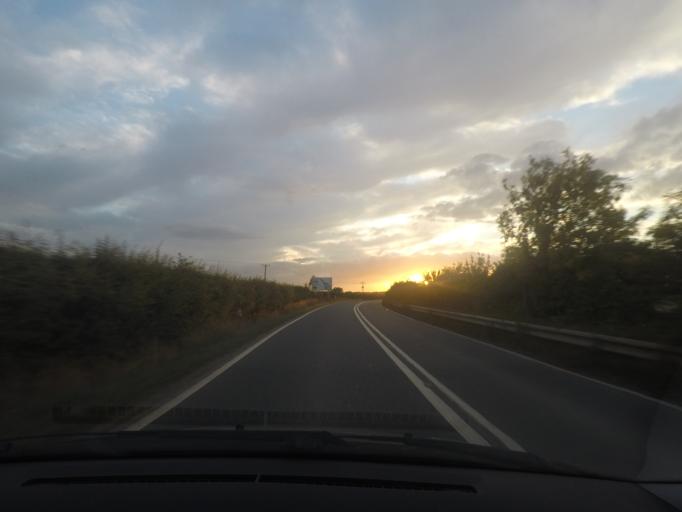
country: GB
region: England
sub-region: North Lincolnshire
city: Croxton
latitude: 53.5850
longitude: -0.3621
